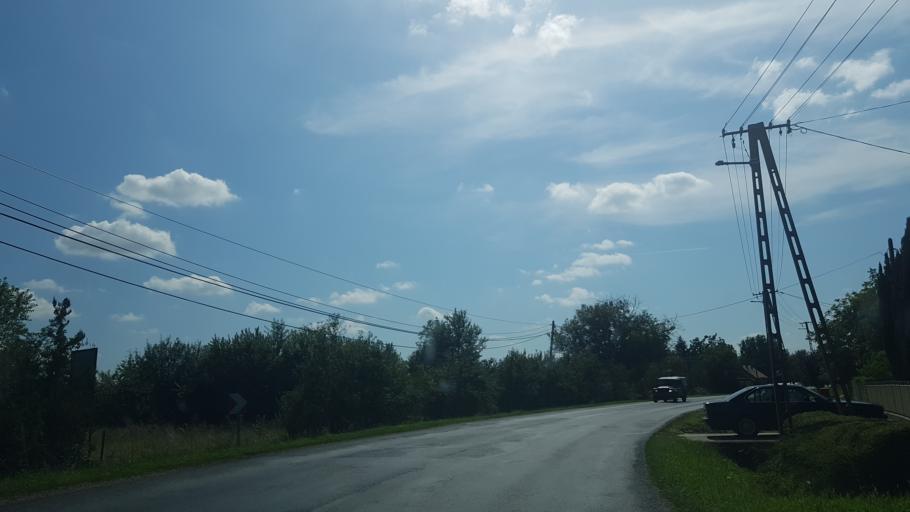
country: HU
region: Somogy
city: Bohonye
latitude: 46.4923
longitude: 17.4237
